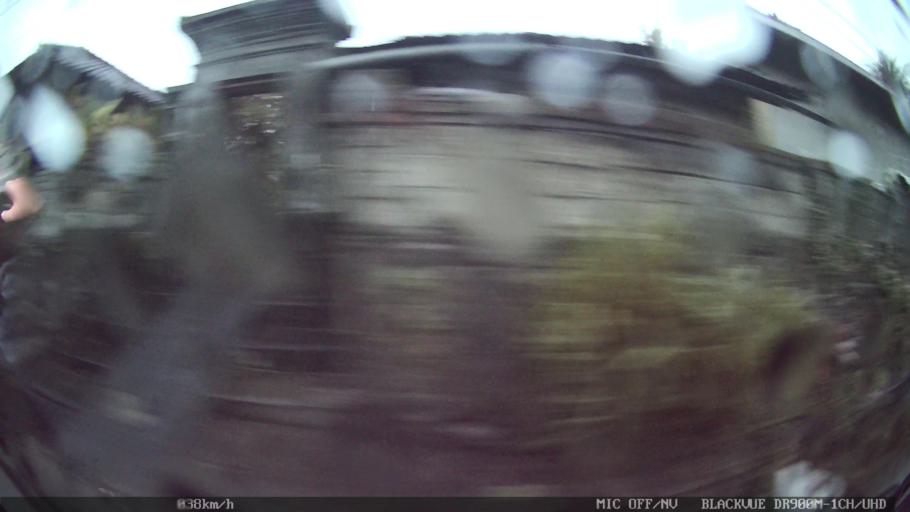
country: ID
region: Bali
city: Banjar Sedang
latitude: -8.5675
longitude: 115.2537
